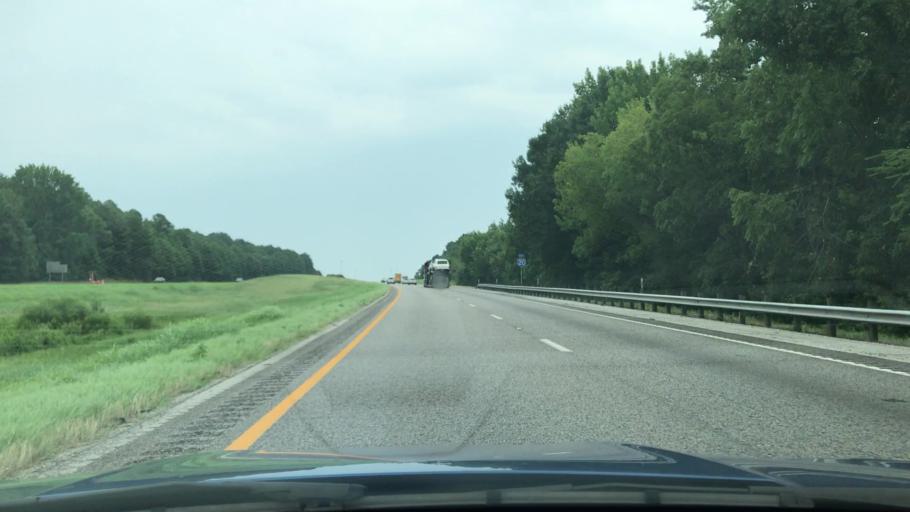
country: US
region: Texas
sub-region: Smith County
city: Tyler
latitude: 32.4559
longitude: -95.3022
